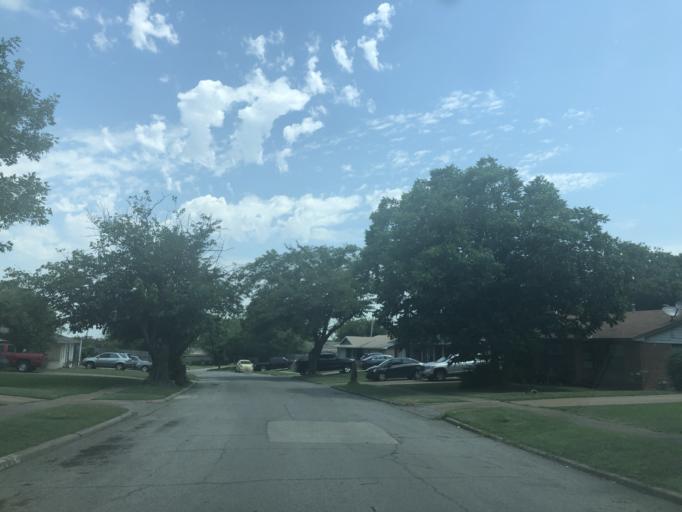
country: US
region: Texas
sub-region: Dallas County
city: Grand Prairie
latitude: 32.7223
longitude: -97.0139
